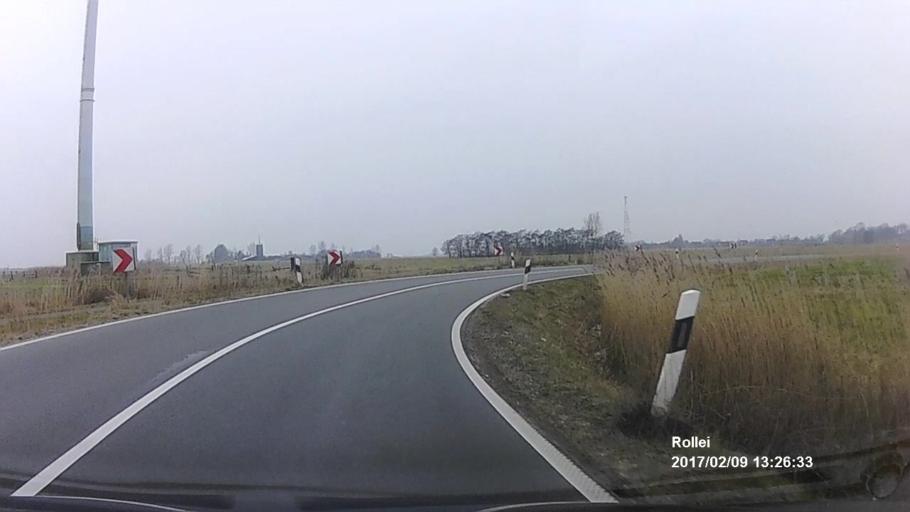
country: DE
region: Lower Saxony
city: Wirdum
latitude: 53.4801
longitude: 7.1362
